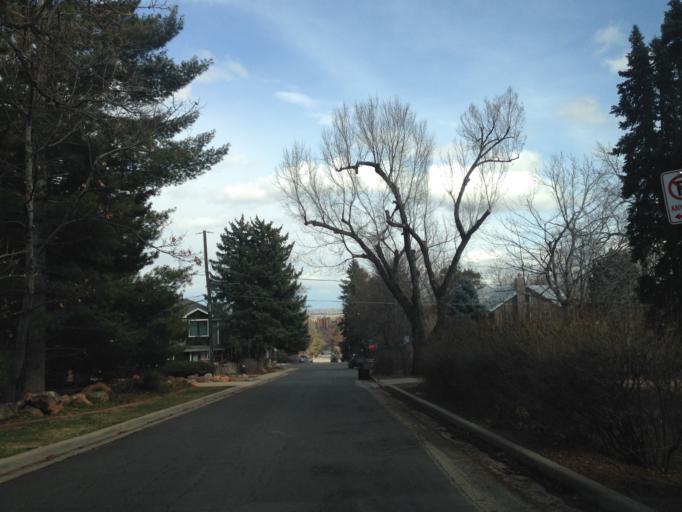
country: US
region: Colorado
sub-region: Boulder County
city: Boulder
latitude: 39.9991
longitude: -105.2749
